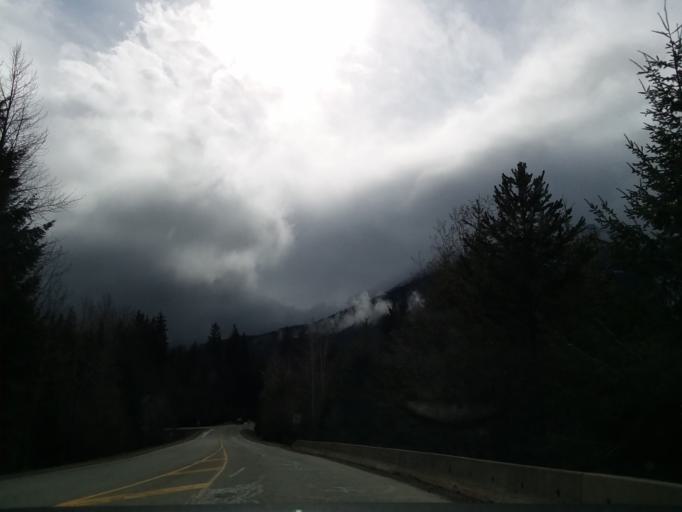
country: CA
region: British Columbia
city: Whistler
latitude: 50.1273
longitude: -122.9653
